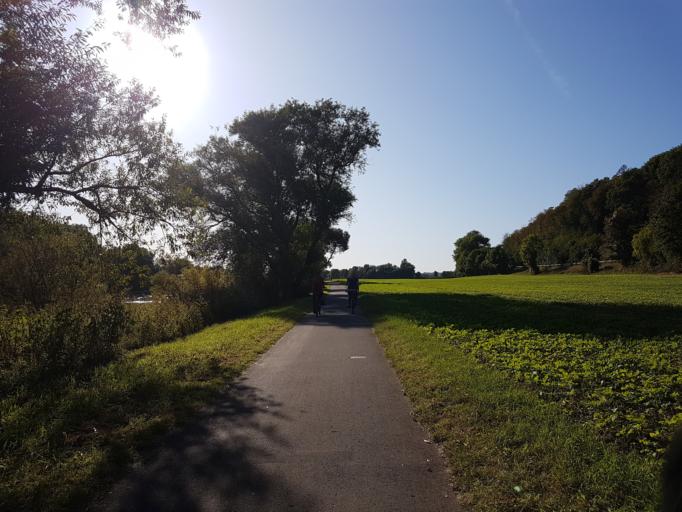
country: DE
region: North Rhine-Westphalia
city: Porta Westfalica
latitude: 52.2411
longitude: 8.9053
